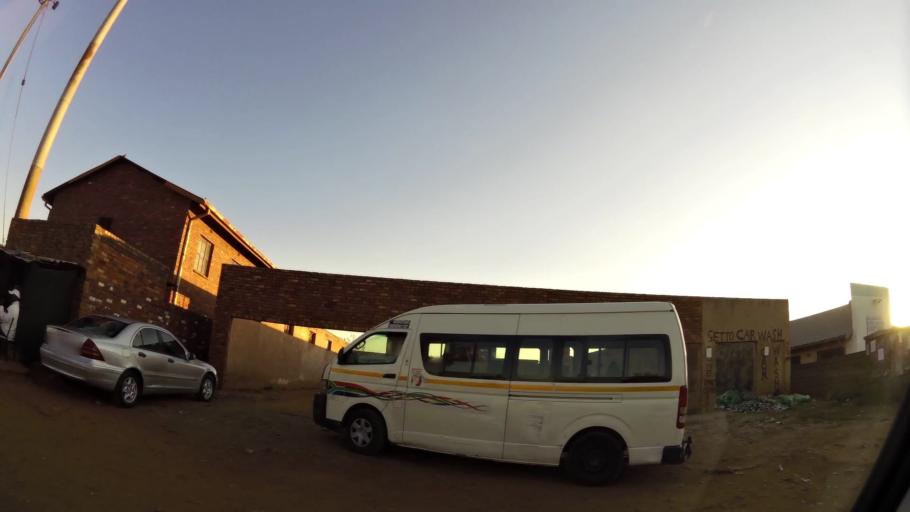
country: ZA
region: Gauteng
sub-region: City of Tshwane Metropolitan Municipality
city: Cullinan
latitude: -25.7098
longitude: 28.3893
